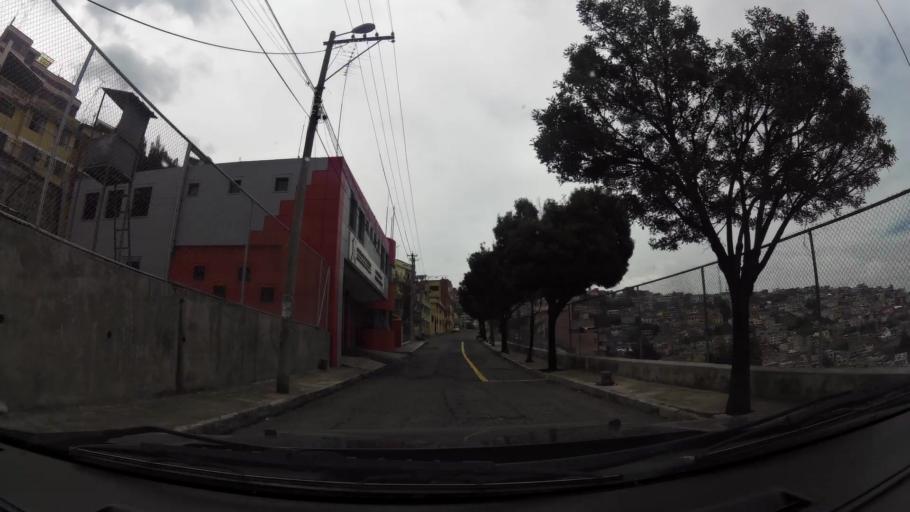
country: EC
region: Pichincha
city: Quito
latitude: -0.2131
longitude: -78.5192
